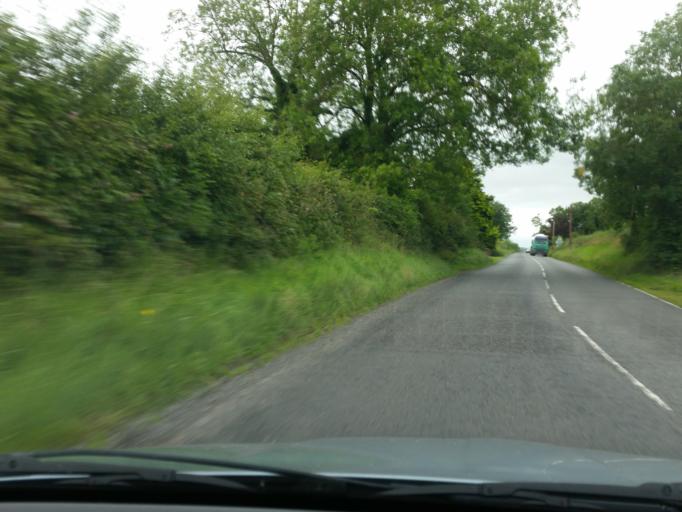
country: GB
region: Northern Ireland
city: Lisnaskea
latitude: 54.1980
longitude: -7.4969
